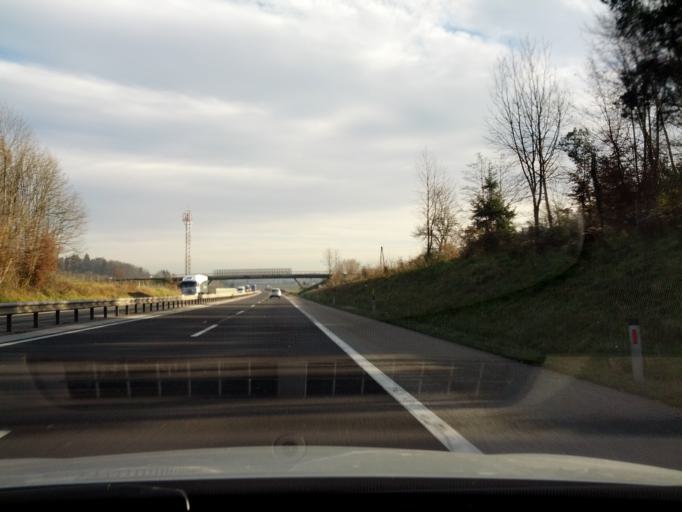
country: SI
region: Slovenska Bistrica
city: Slovenska Bistrica
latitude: 46.3737
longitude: 15.5435
